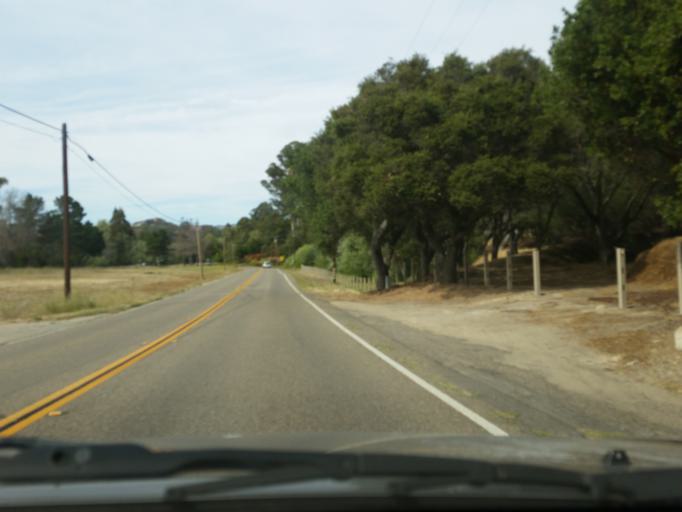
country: US
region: California
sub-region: San Luis Obispo County
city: Arroyo Grande
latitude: 35.1313
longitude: -120.5709
